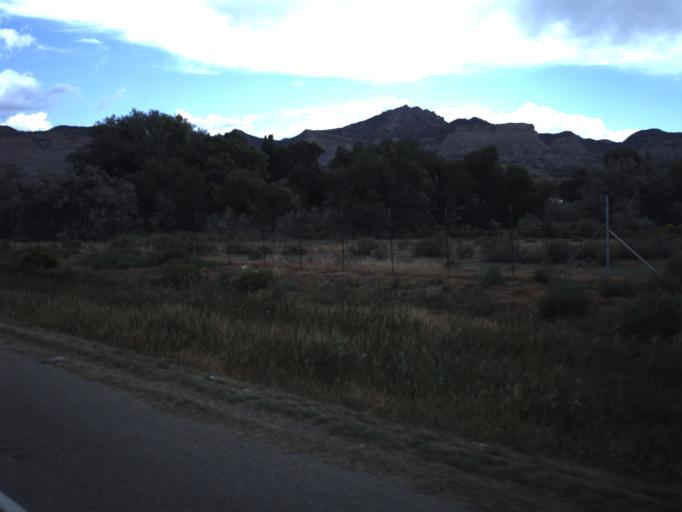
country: US
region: Utah
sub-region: Carbon County
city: Spring Glen
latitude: 39.6580
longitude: -110.8606
